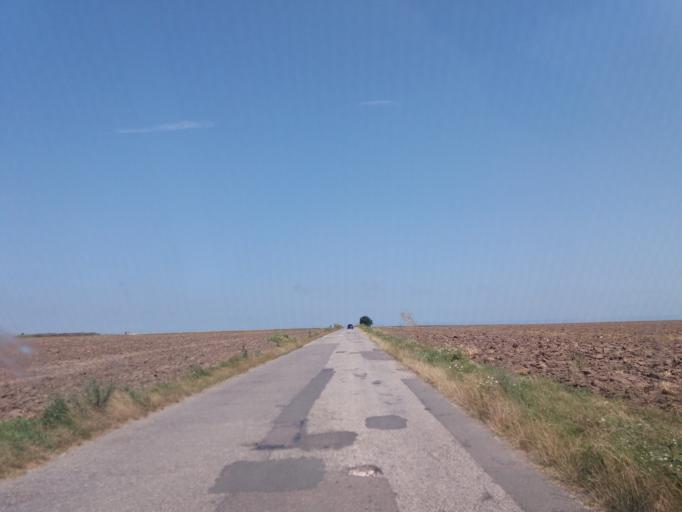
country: RO
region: Constanta
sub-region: Comuna Corbu
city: Corbu
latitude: 44.4239
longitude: 28.6796
